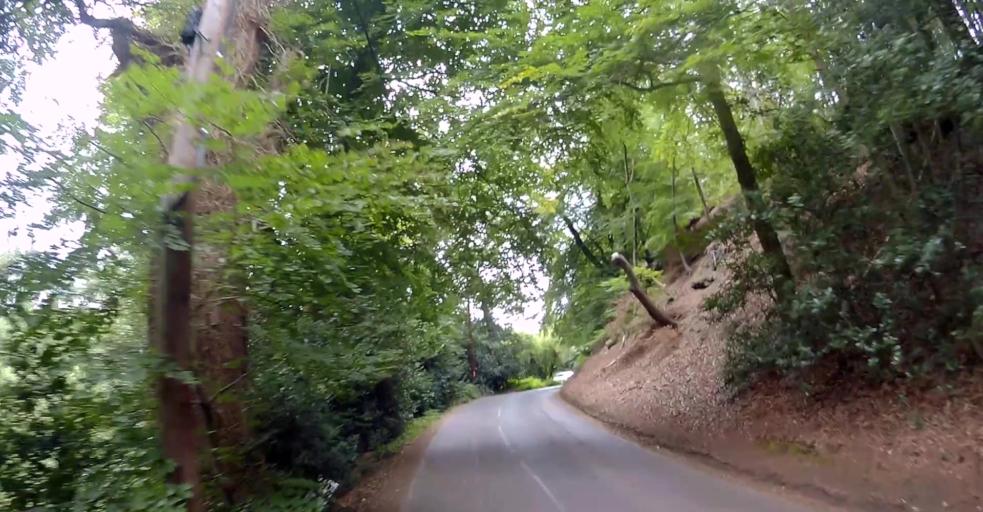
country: GB
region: England
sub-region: Surrey
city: Hale
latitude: 51.2120
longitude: -0.7716
